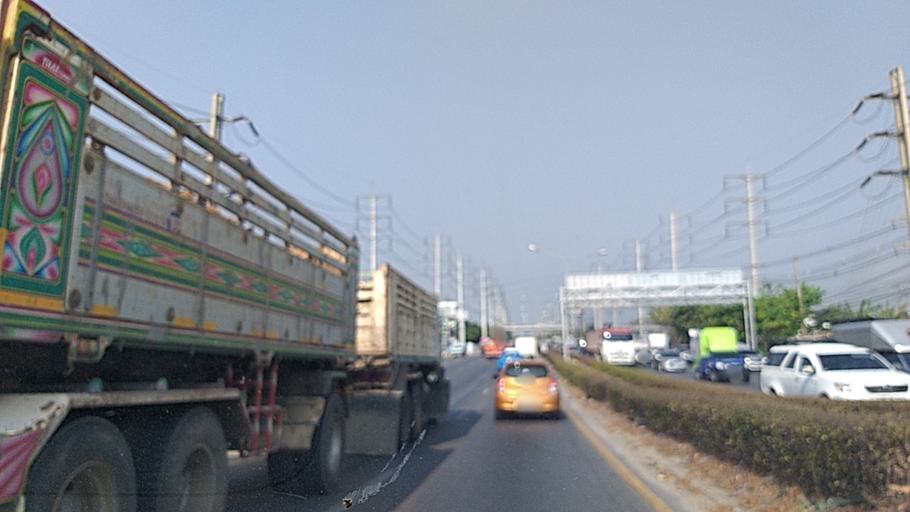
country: TH
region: Pathum Thani
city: Lam Luk Ka
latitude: 13.9336
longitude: 100.7055
